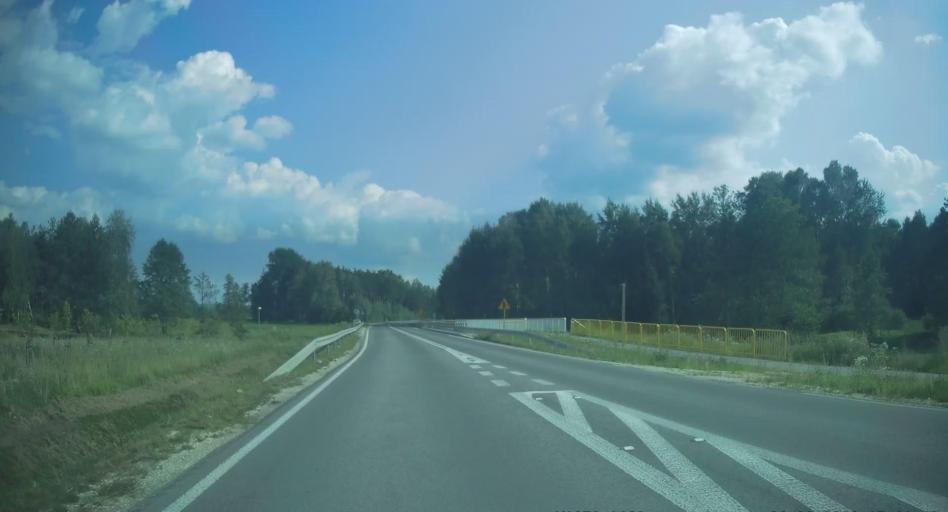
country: PL
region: Swietokrzyskie
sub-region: Powiat konecki
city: Radoszyce
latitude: 51.0609
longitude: 20.2766
